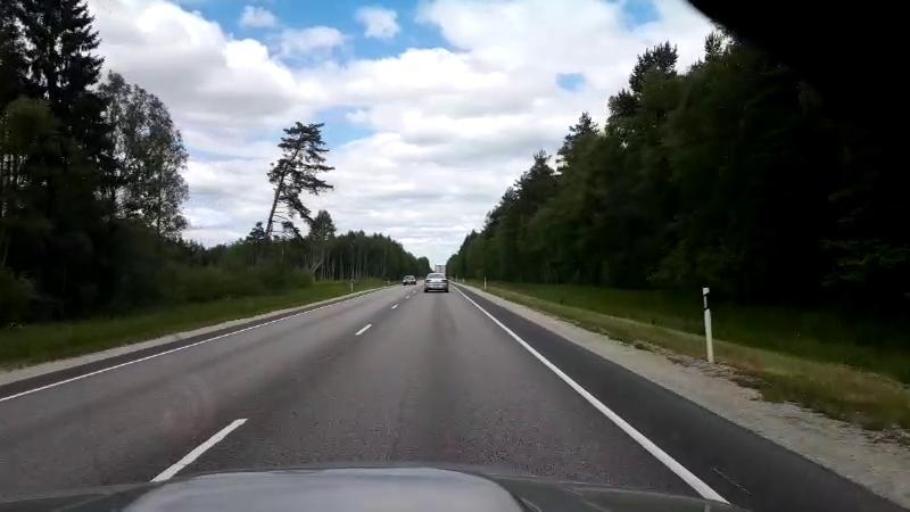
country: EE
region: Paernumaa
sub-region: Halinga vald
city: Parnu-Jaagupi
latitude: 58.7217
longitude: 24.4237
